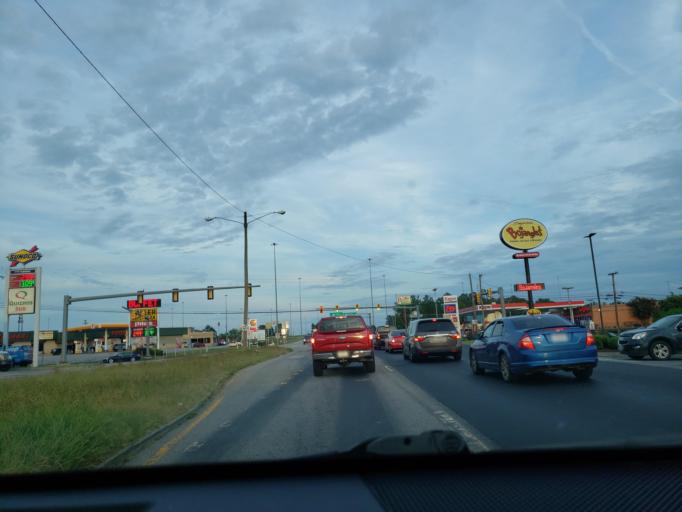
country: US
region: Virginia
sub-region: City of Emporia
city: Emporia
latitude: 36.7045
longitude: -77.5544
